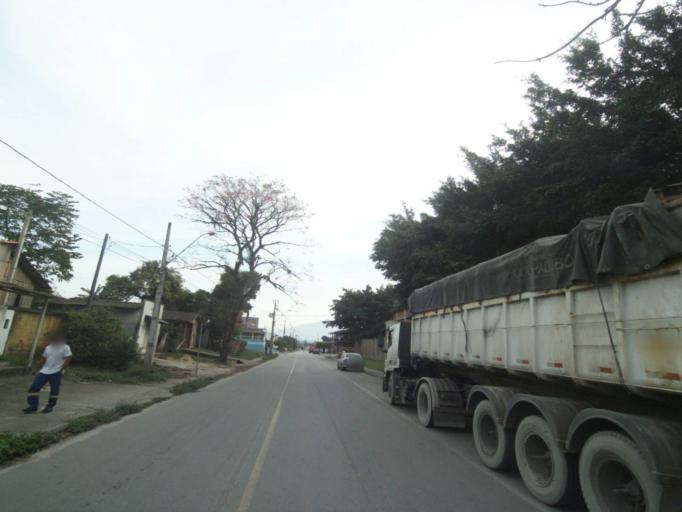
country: BR
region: Parana
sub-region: Paranagua
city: Paranagua
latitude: -25.5214
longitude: -48.5362
